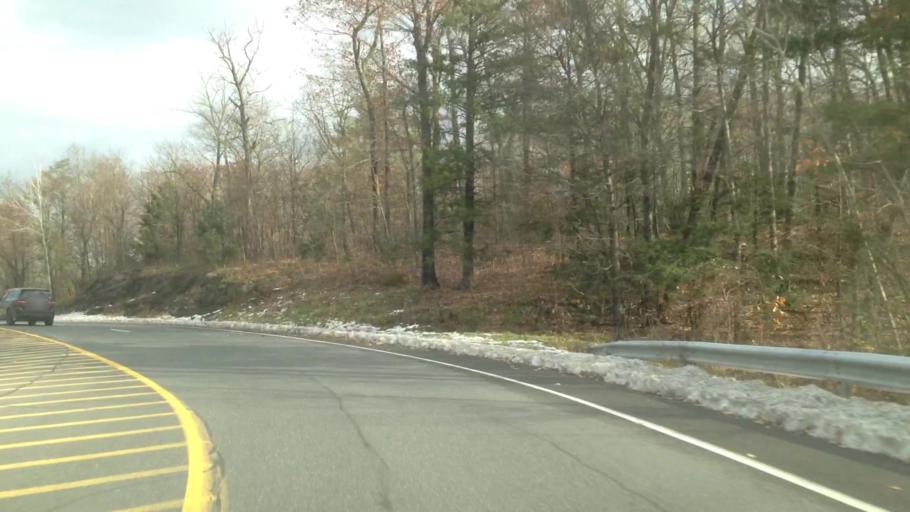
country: US
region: New York
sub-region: Ulster County
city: Lincoln Park
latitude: 41.9593
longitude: -73.9843
